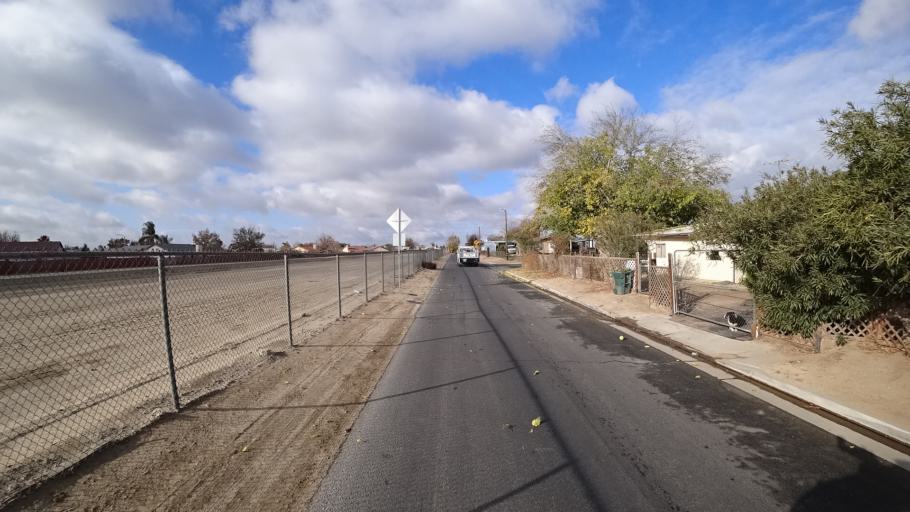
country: US
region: California
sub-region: Kern County
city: Greenfield
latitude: 35.2922
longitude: -119.0082
